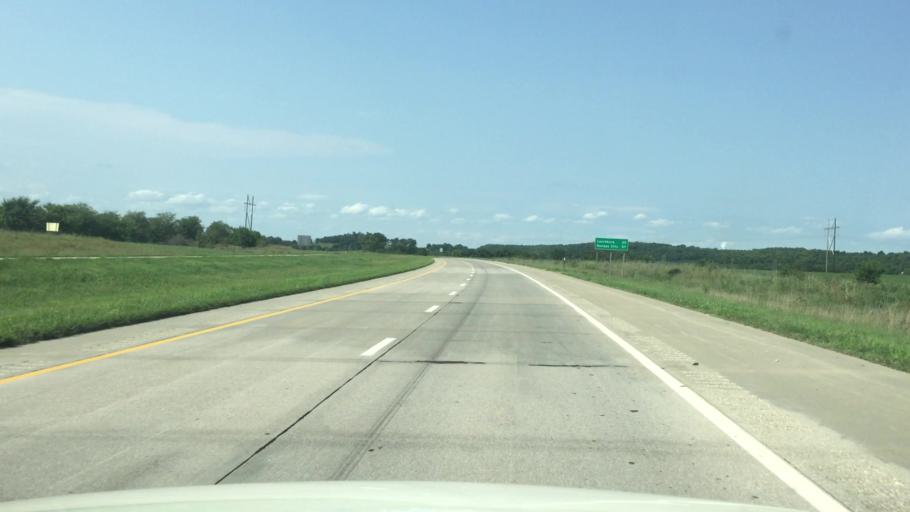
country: US
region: Kansas
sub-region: Linn County
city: Pleasanton
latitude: 38.2728
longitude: -94.6680
